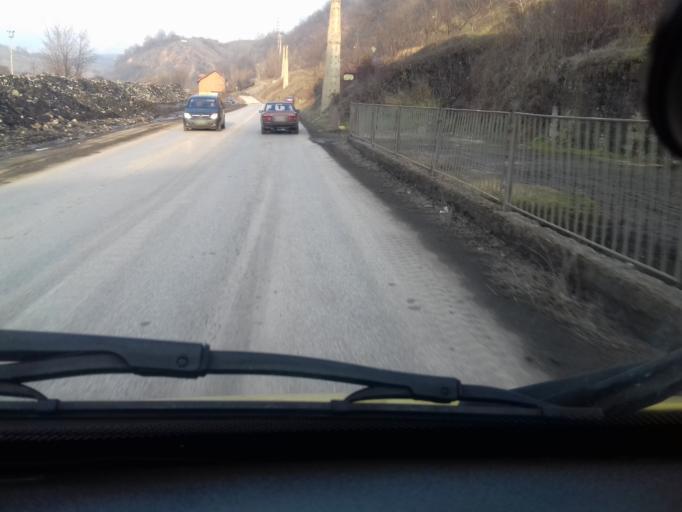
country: BA
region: Federation of Bosnia and Herzegovina
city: Kakanj
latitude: 44.1065
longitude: 18.1173
